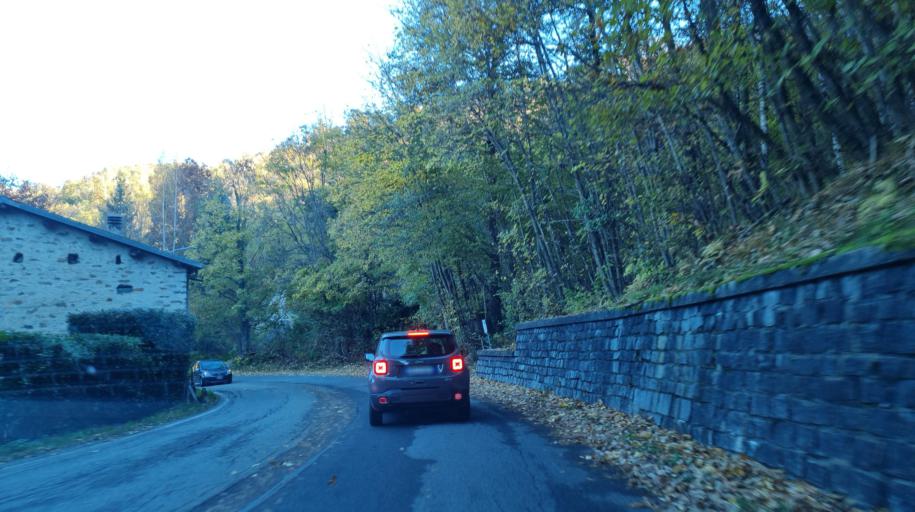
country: IT
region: Piedmont
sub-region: Provincia di Torino
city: Alice Superiore
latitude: 45.4751
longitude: 7.7835
